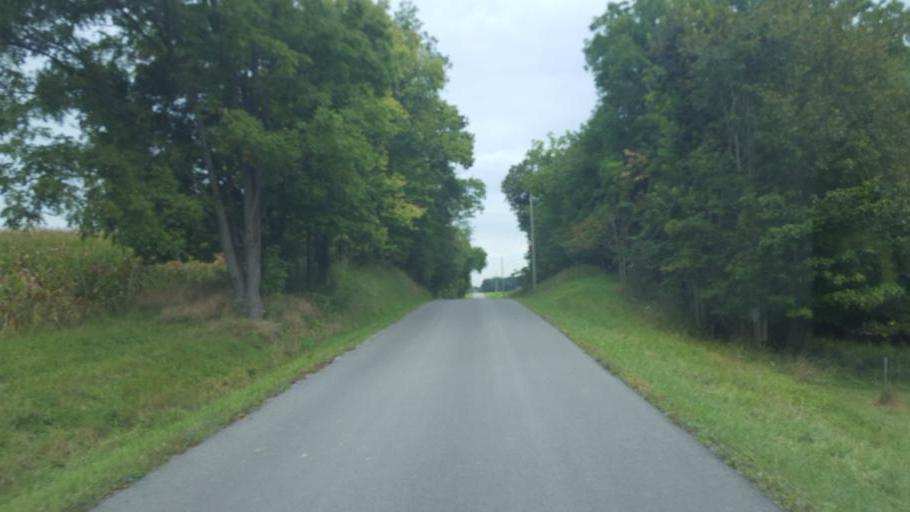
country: US
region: Ohio
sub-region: Wyandot County
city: Upper Sandusky
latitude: 40.7635
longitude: -83.1883
